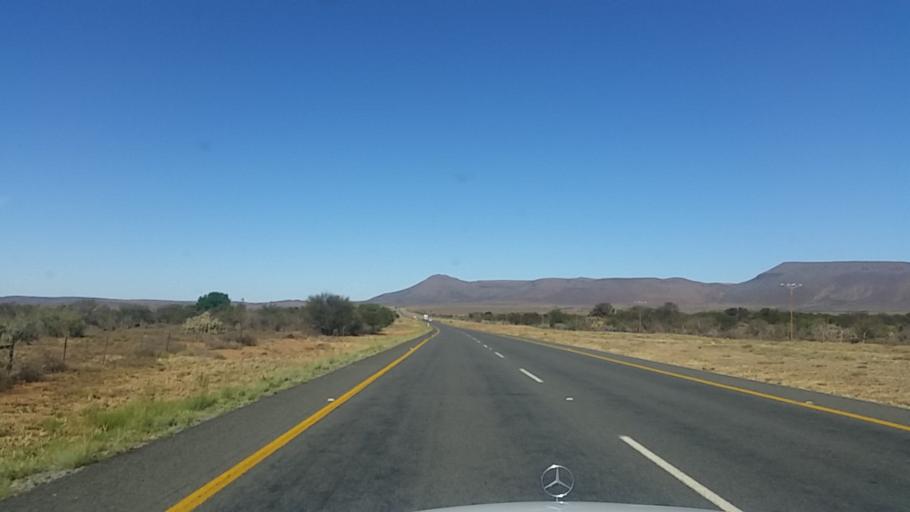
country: ZA
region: Eastern Cape
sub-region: Cacadu District Municipality
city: Graaff-Reinet
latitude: -32.0023
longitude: 24.6646
